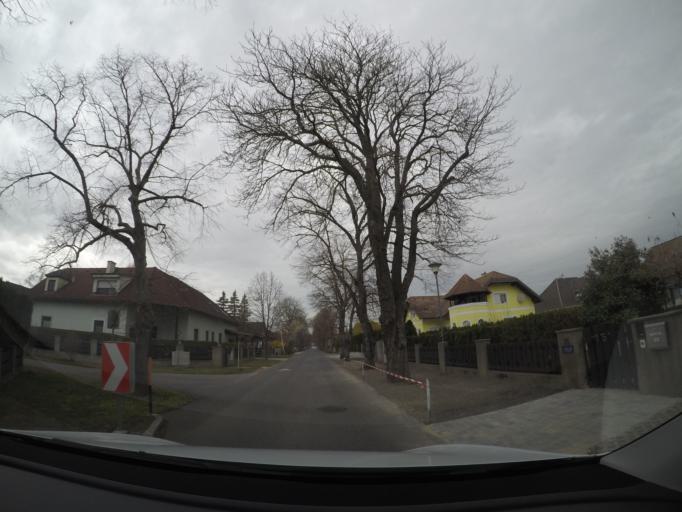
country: AT
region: Lower Austria
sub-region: Politischer Bezirk Baden
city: Ebreichsdorf
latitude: 47.9413
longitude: 16.3992
